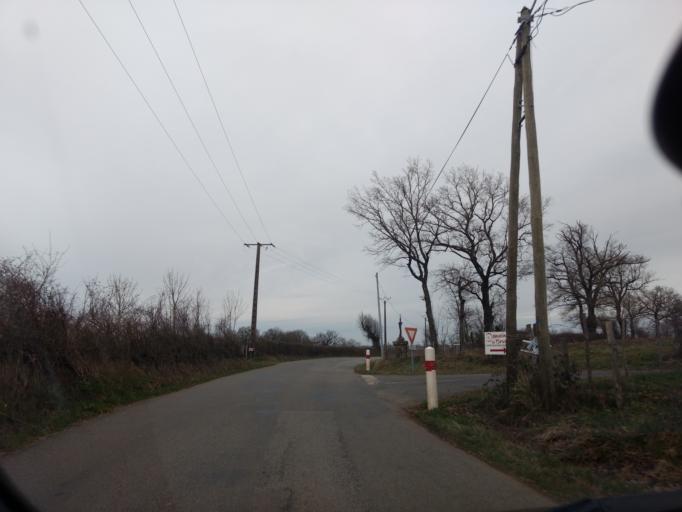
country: FR
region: Midi-Pyrenees
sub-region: Departement de l'Aveyron
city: Saint-Christophe-Vallon
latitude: 44.4353
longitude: 2.3567
